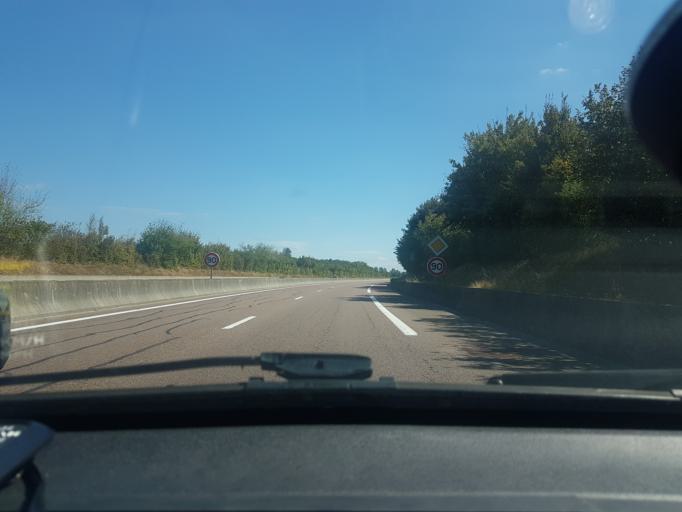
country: FR
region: Bourgogne
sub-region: Departement de la Cote-d'Or
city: Couternon
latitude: 47.3457
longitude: 5.1440
